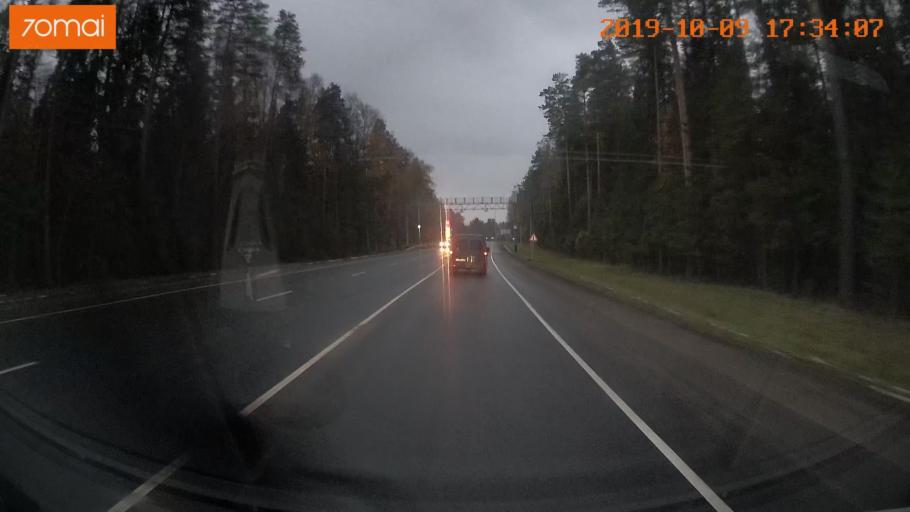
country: RU
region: Ivanovo
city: Bogorodskoye
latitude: 57.1096
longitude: 41.0149
